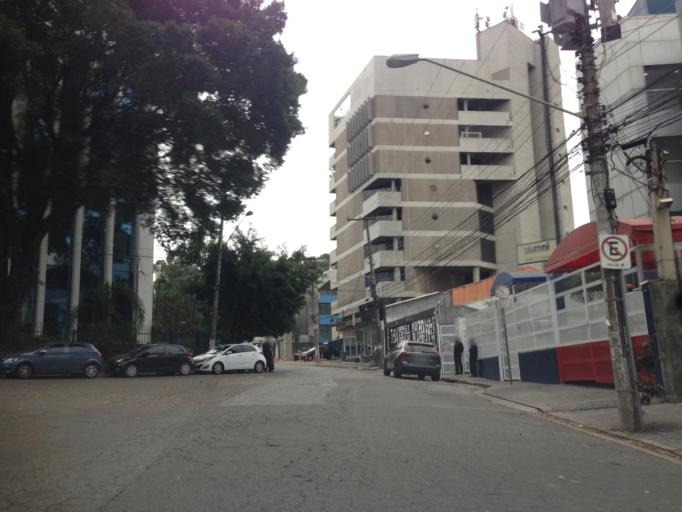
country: BR
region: Sao Paulo
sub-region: Taboao Da Serra
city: Taboao da Serra
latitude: -23.6153
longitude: -46.7027
